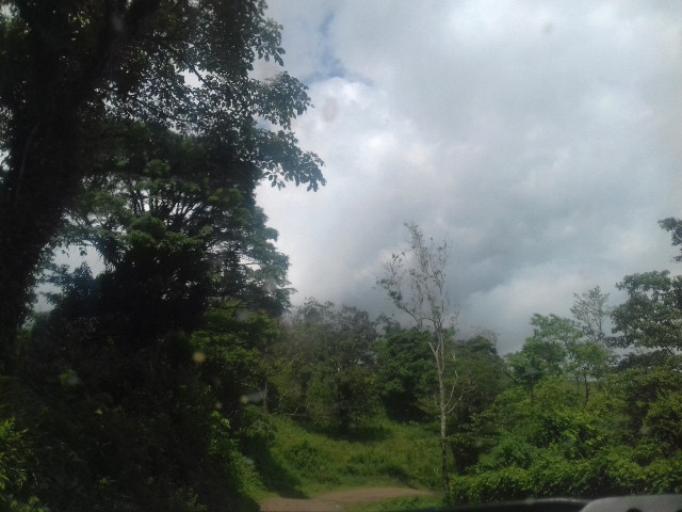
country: NI
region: Matagalpa
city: Matiguas
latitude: 12.9341
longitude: -85.3688
